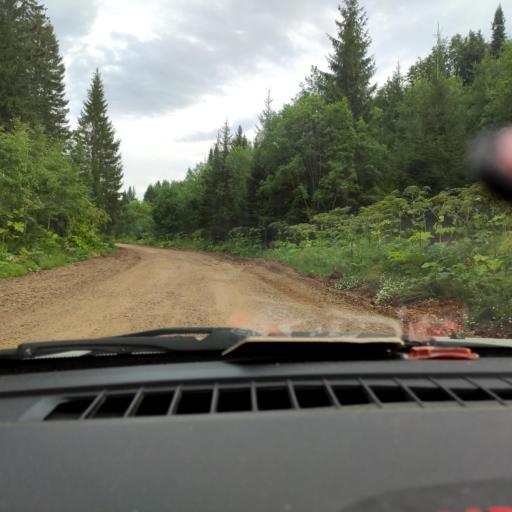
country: RU
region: Perm
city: Kultayevo
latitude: 57.8147
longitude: 56.0011
